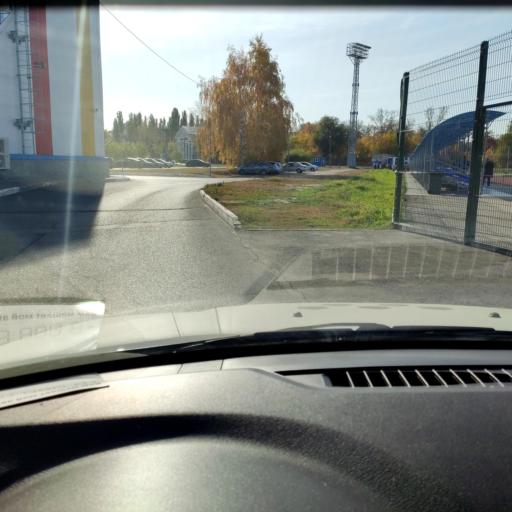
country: RU
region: Samara
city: Tol'yatti
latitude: 53.5144
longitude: 49.4065
